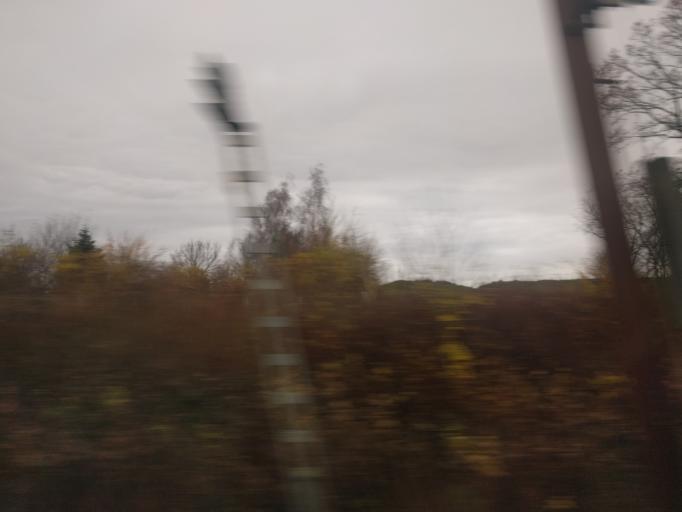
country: DK
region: Zealand
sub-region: Ringsted Kommune
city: Ringsted
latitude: 55.4398
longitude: 11.8220
